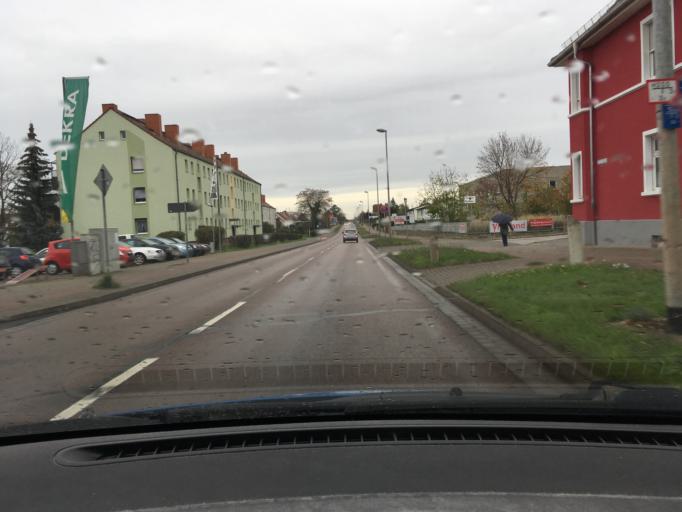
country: DE
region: Saxony-Anhalt
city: Rosslau
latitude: 51.8889
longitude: 12.2315
